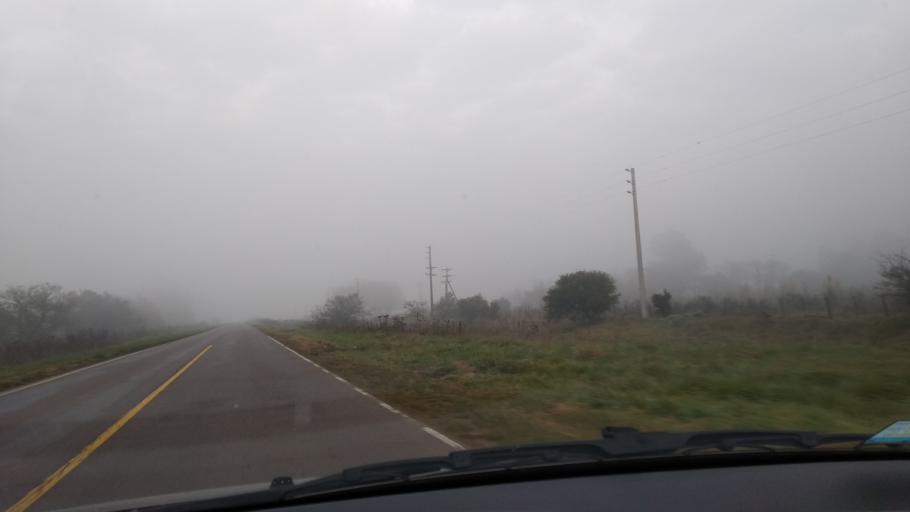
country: AR
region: Buenos Aires
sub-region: Partido de San Vicente
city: San Vicente
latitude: -35.2371
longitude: -58.4680
